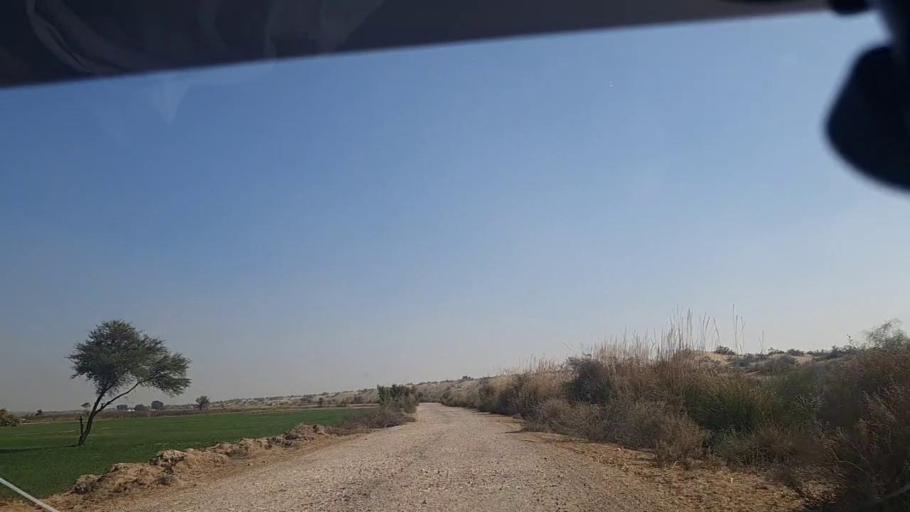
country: PK
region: Sindh
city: Khanpur
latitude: 27.5600
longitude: 69.3256
